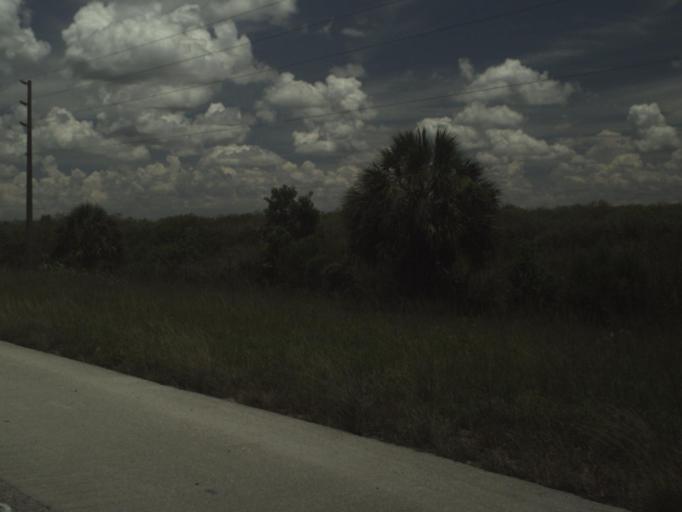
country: US
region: Florida
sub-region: Broward County
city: Weston
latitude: 26.1568
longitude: -80.7673
